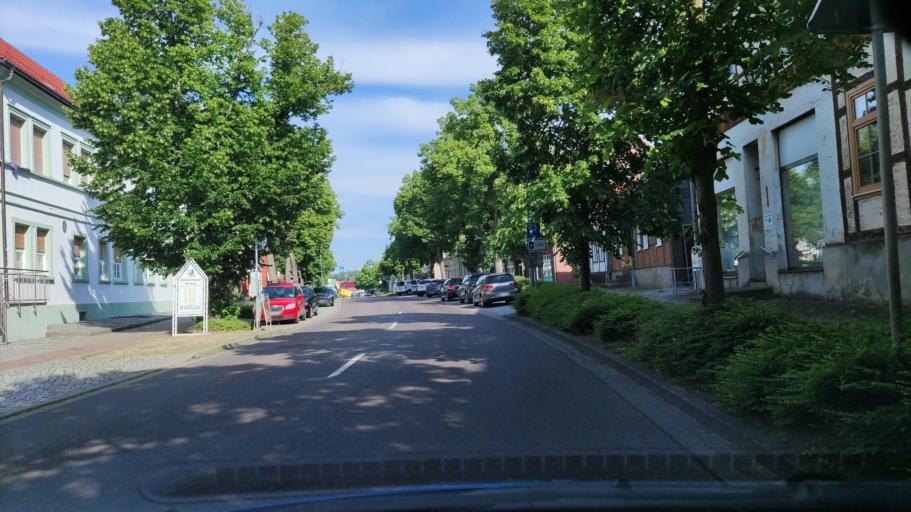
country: DE
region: Saxony-Anhalt
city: Klotze
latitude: 52.6256
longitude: 11.1630
